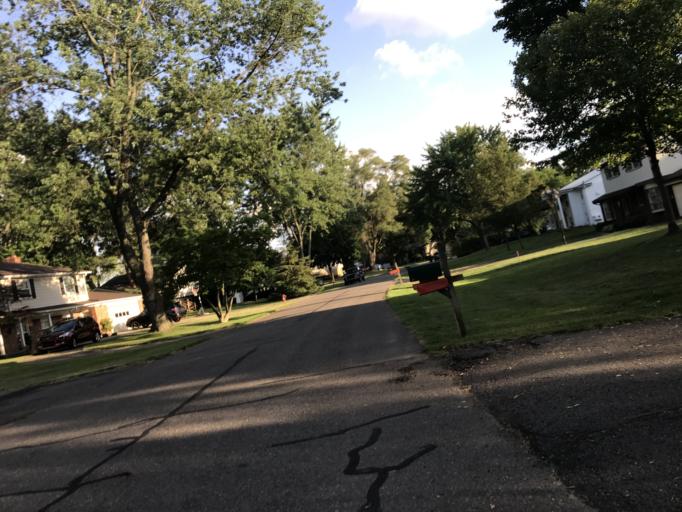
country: US
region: Michigan
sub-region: Oakland County
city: Farmington Hills
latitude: 42.4885
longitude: -83.3410
